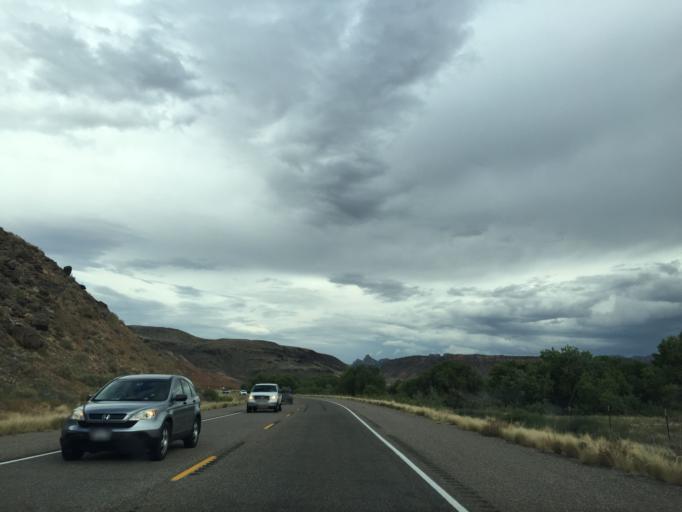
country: US
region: Utah
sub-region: Washington County
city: LaVerkin
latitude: 37.1806
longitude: -113.1280
